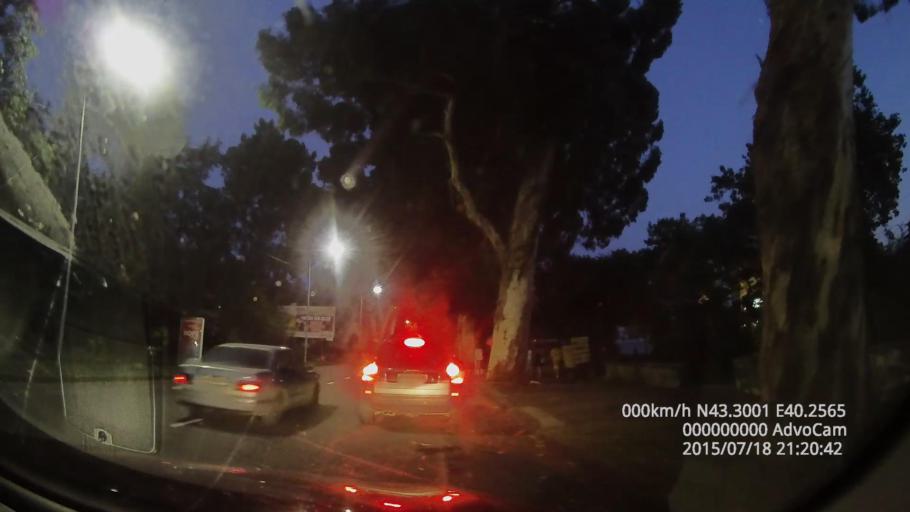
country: GE
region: Abkhazia
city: Gagra
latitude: 43.3001
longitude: 40.2565
